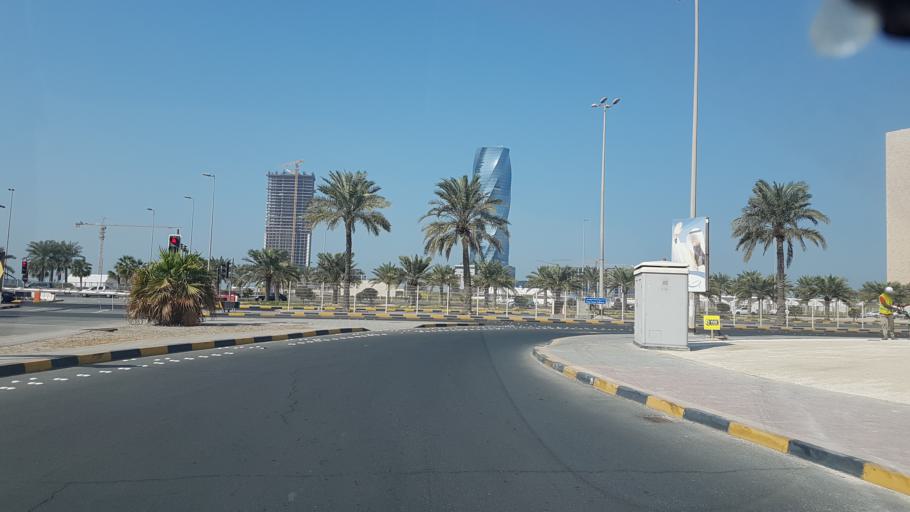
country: BH
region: Manama
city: Manama
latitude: 26.2392
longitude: 50.5802
